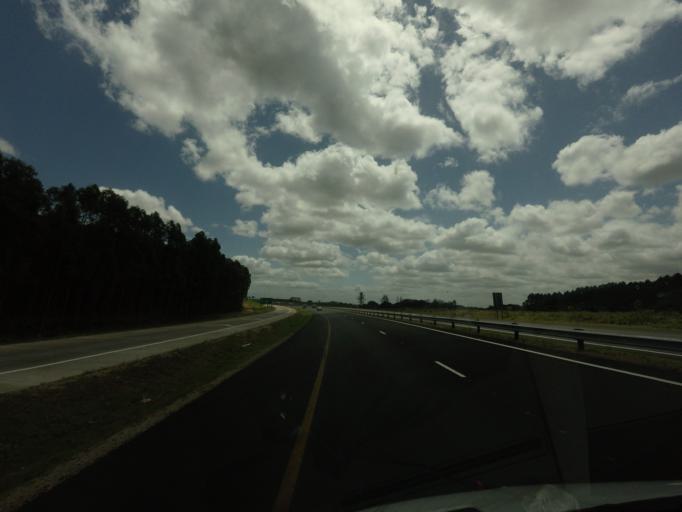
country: ZA
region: KwaZulu-Natal
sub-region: uThungulu District Municipality
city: KwaMbonambi
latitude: -28.5268
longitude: 32.1375
